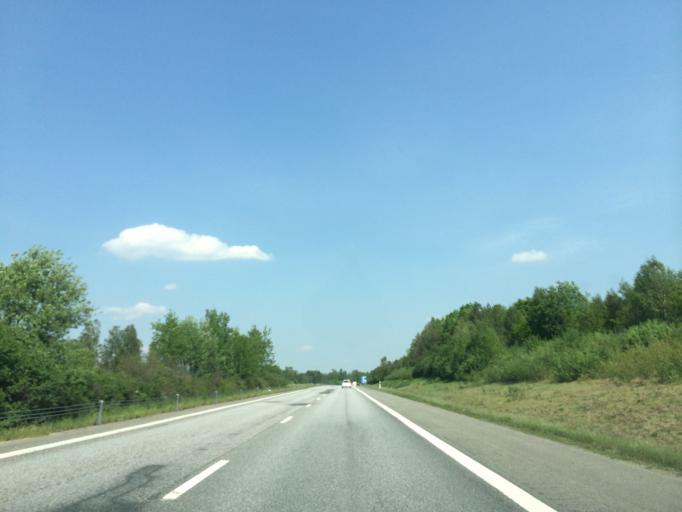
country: SE
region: Joenkoeping
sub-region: Varnamo Kommun
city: Varnamo
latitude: 57.1330
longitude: 14.0617
